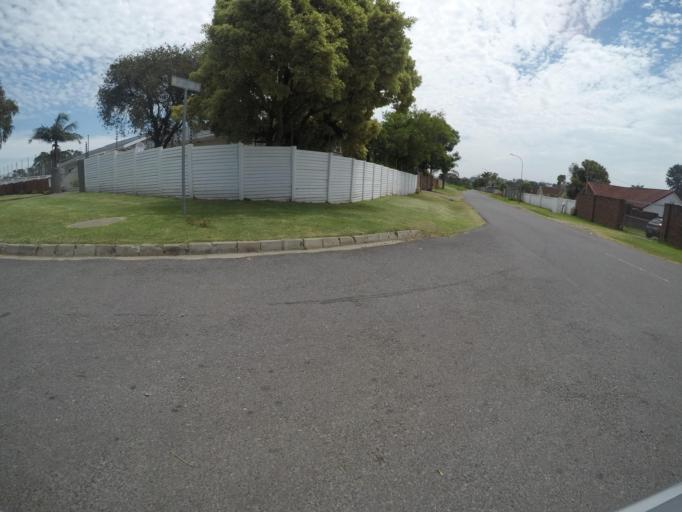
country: ZA
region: Eastern Cape
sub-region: Buffalo City Metropolitan Municipality
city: East London
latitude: -32.9827
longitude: 27.8631
